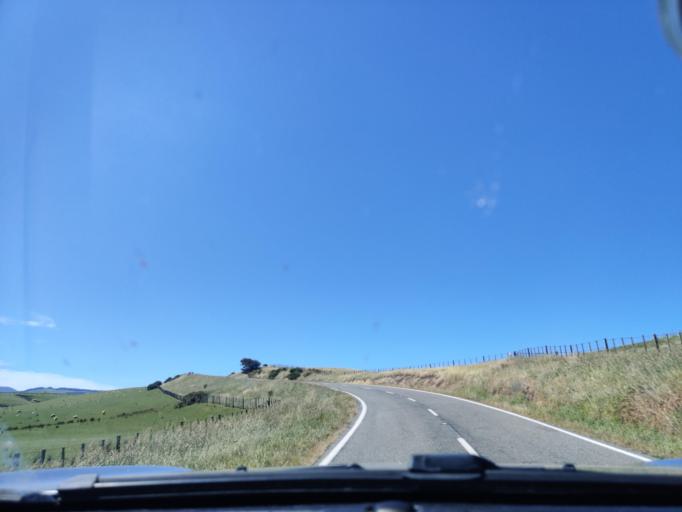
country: NZ
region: Wellington
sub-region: Upper Hutt City
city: Upper Hutt
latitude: -41.3756
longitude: 175.1783
